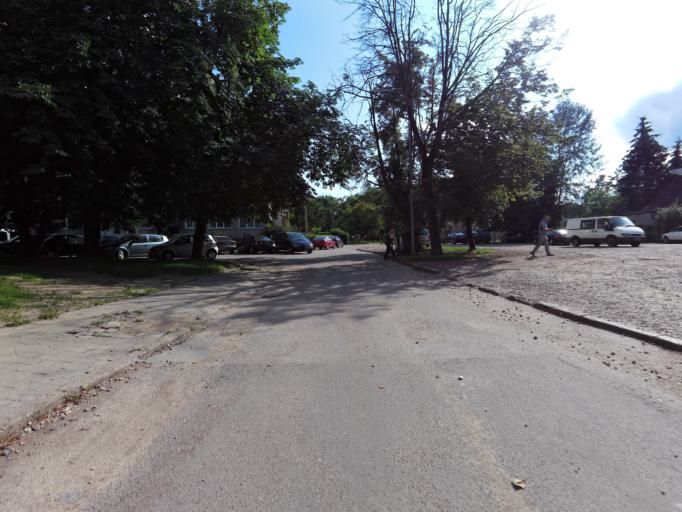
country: LT
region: Vilnius County
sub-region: Vilnius
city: Vilnius
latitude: 54.7032
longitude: 25.2958
